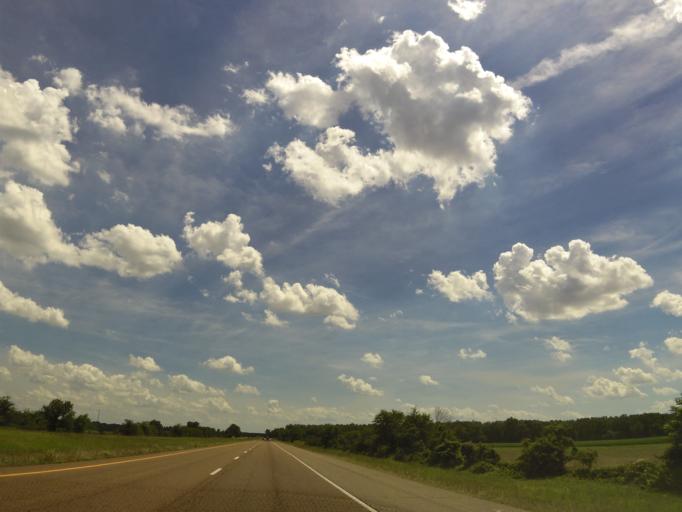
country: US
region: Tennessee
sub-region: Dyer County
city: Dyersburg
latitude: 36.0432
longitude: -89.3368
